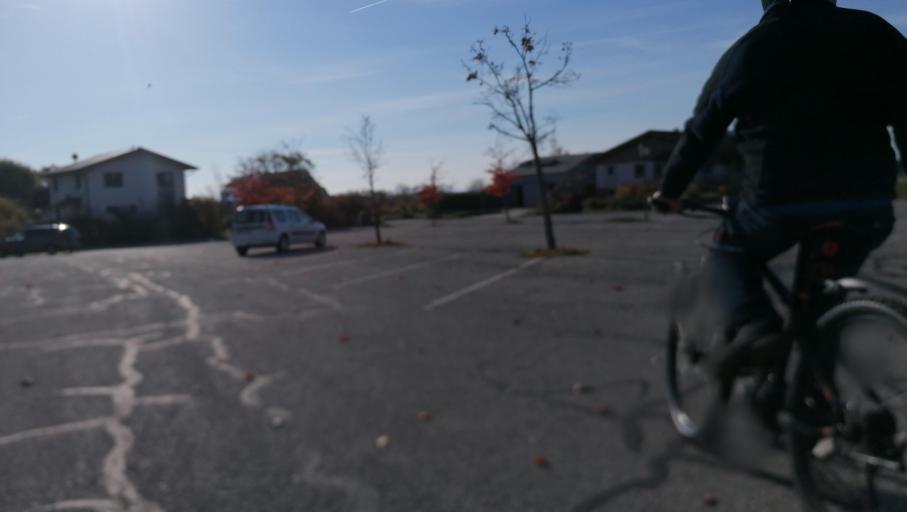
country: AT
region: Lower Austria
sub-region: Politischer Bezirk Modling
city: Gumpoldskirchen
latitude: 48.0418
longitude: 16.2783
